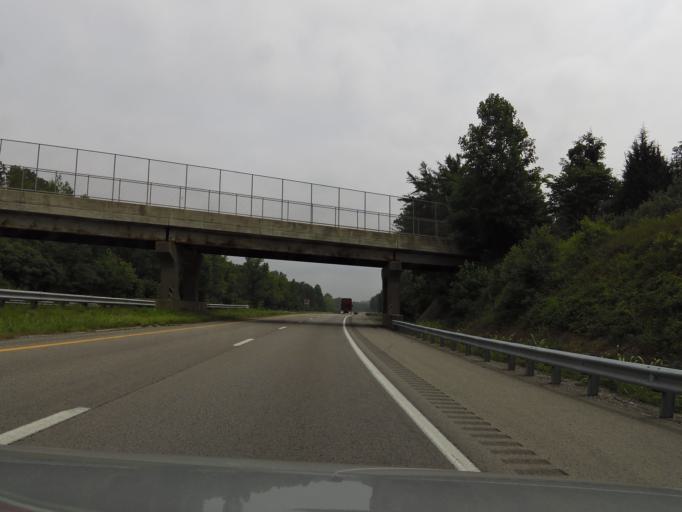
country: US
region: Kentucky
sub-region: Muhlenberg County
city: Central City
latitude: 37.3082
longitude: -87.0609
